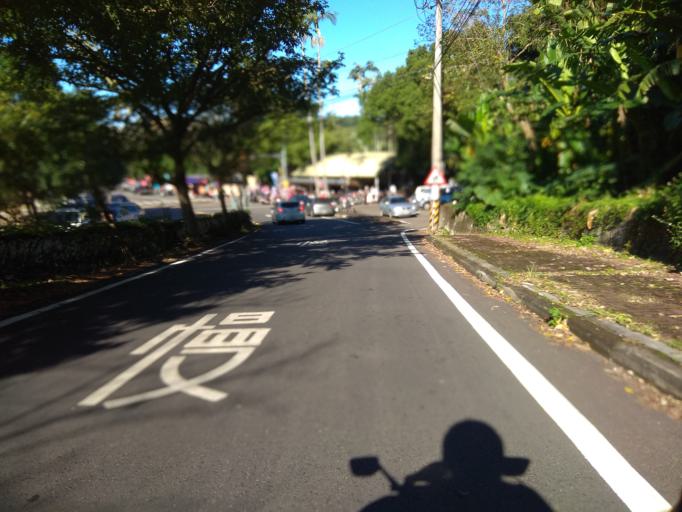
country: TW
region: Taiwan
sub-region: Hsinchu
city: Zhubei
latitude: 24.8464
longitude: 121.1183
